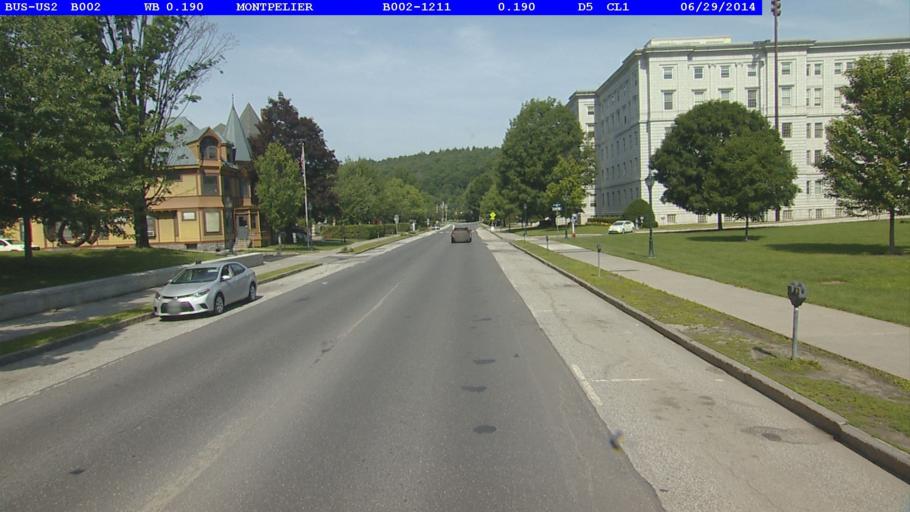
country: US
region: Vermont
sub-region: Washington County
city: Montpelier
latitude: 44.2614
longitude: -72.5810
